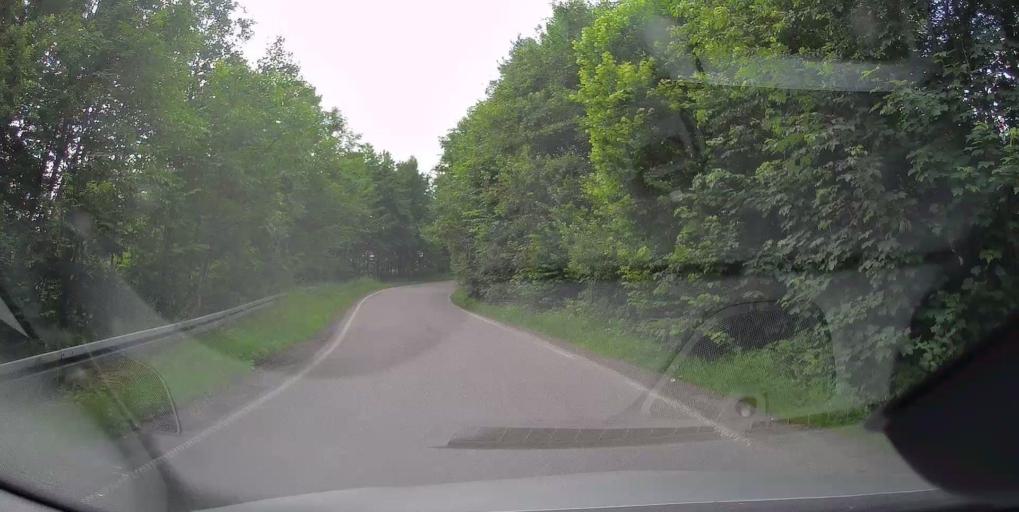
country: PL
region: Lesser Poland Voivodeship
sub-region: Powiat nowosadecki
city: Korzenna
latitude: 49.7127
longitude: 20.7738
